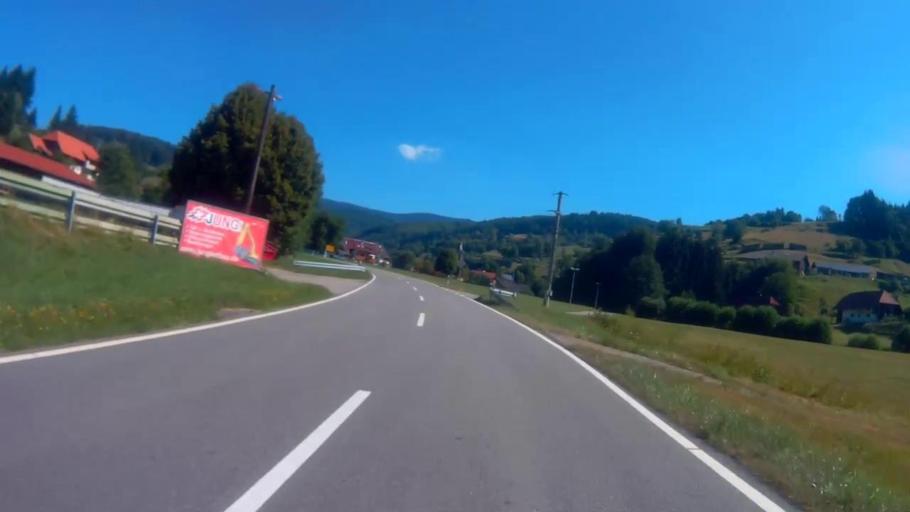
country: DE
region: Baden-Wuerttemberg
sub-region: Freiburg Region
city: Bollen
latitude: 47.7454
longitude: 7.7672
